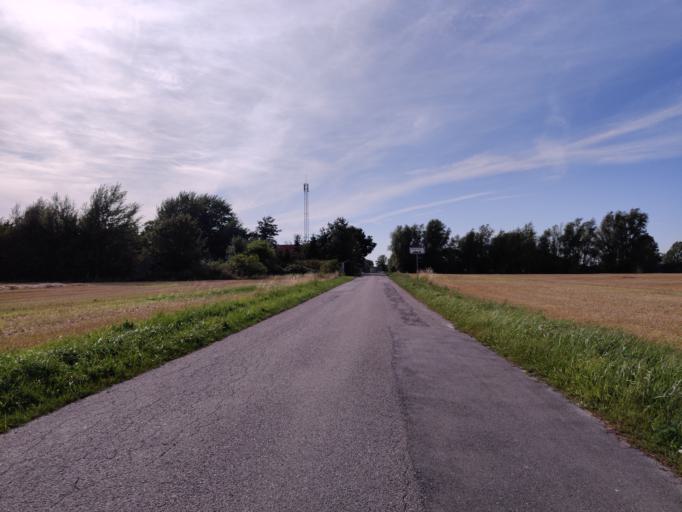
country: DK
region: Zealand
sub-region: Guldborgsund Kommune
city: Nykobing Falster
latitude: 54.6531
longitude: 11.9035
